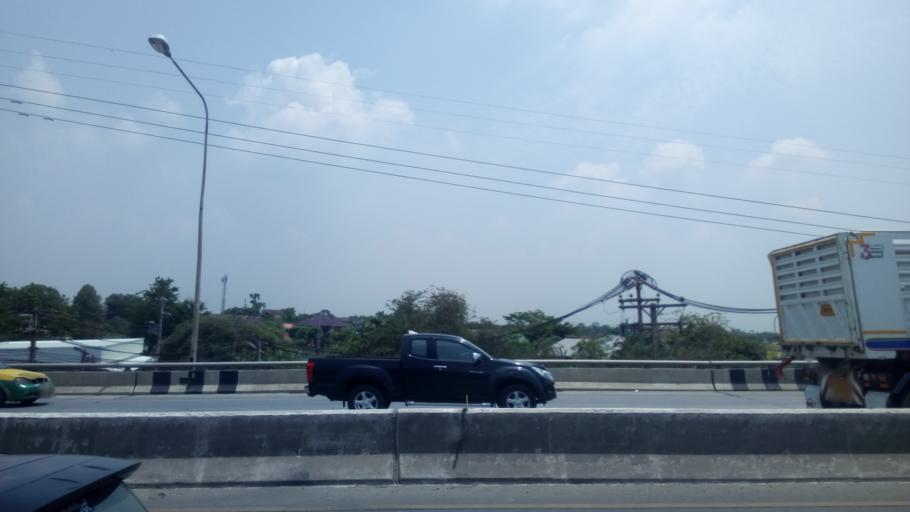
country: TH
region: Pathum Thani
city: Pathum Thani
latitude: 14.0268
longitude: 100.5379
